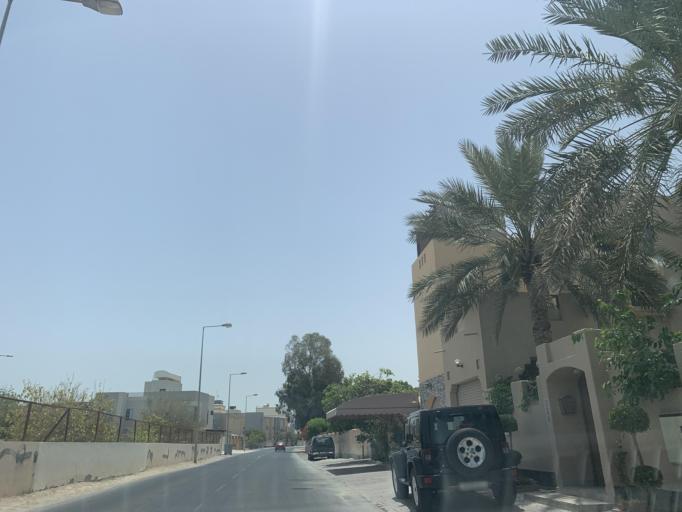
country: BH
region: Northern
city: Madinat `Isa
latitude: 26.1727
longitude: 50.5706
